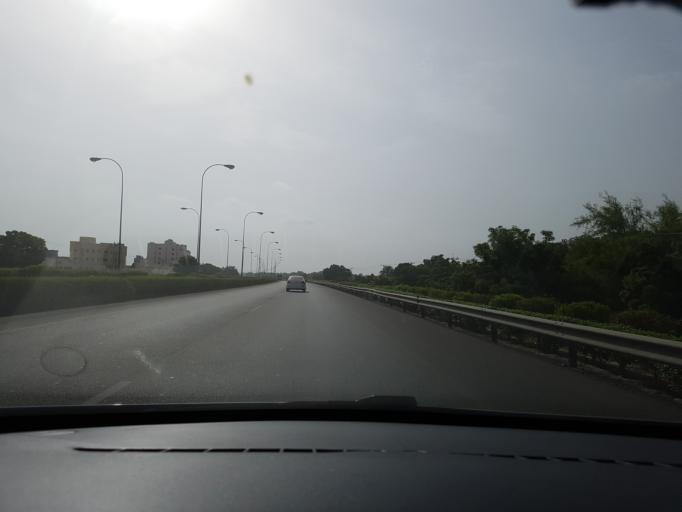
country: OM
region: Al Batinah
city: Al Sohar
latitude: 24.3970
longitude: 56.6711
